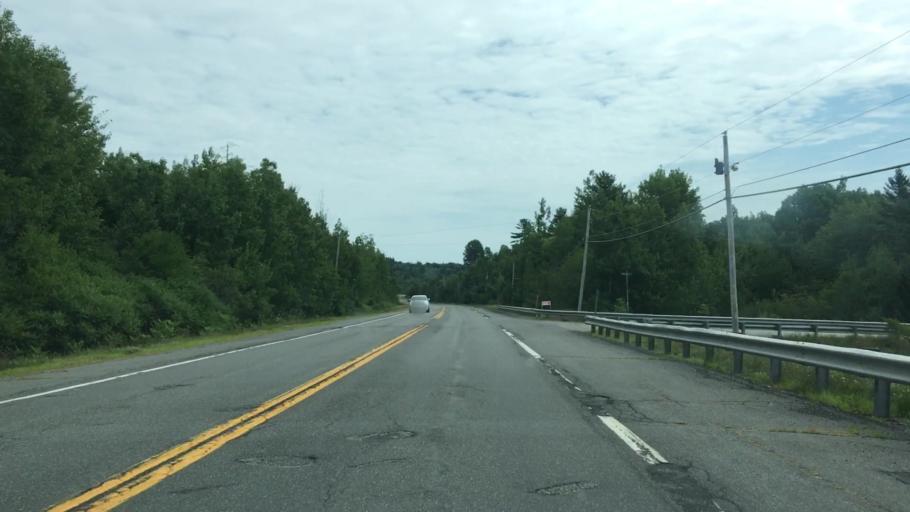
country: US
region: Maine
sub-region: Washington County
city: Calais
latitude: 45.1136
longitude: -67.4119
